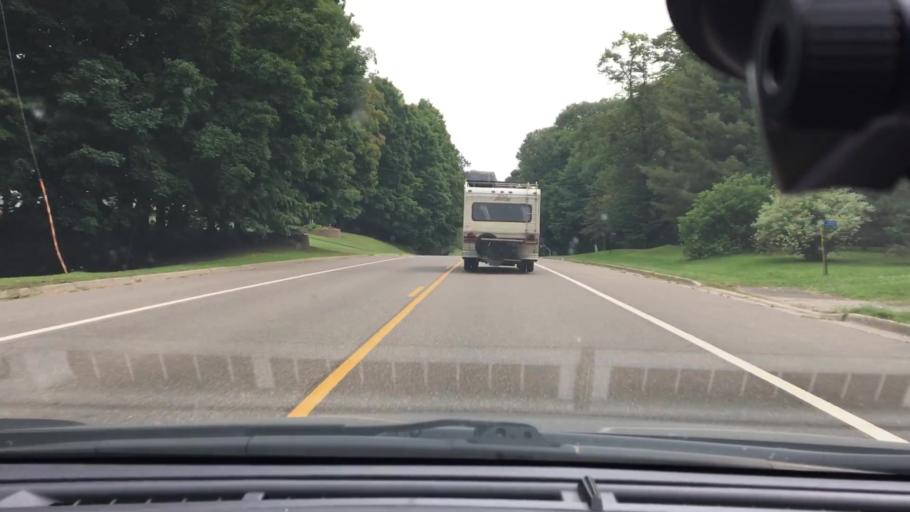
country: US
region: Minnesota
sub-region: Crow Wing County
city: Crosby
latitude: 46.4103
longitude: -93.8623
